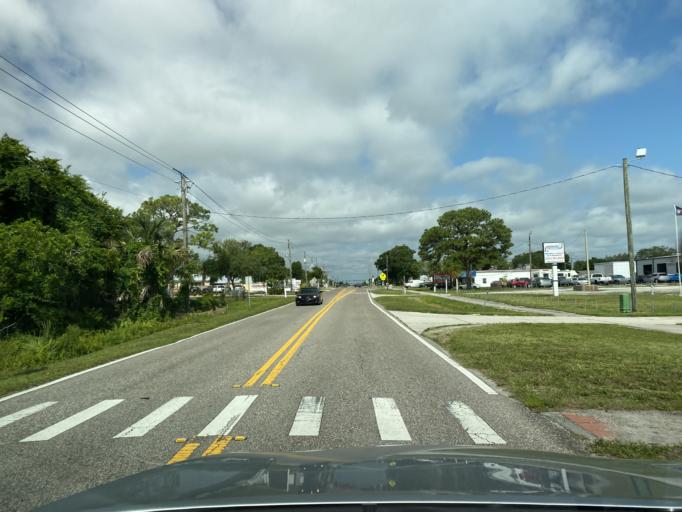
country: US
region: Florida
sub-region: Brevard County
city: Palm Bay
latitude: 28.0345
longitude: -80.5909
